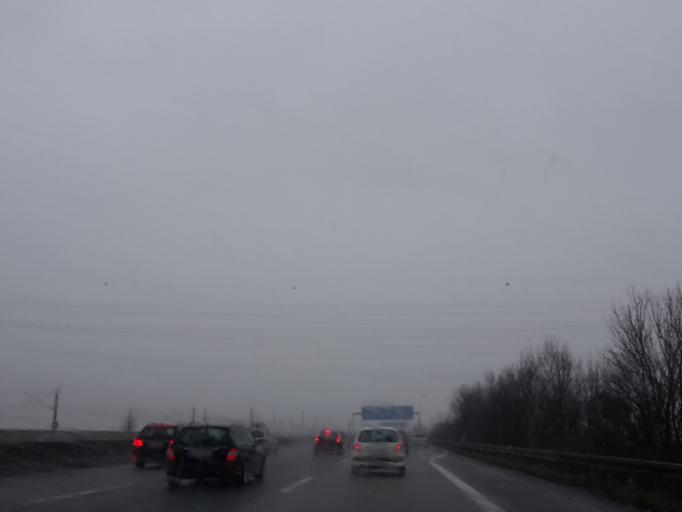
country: DE
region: Hesse
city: Raunheim
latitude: 50.0336
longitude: 8.4452
